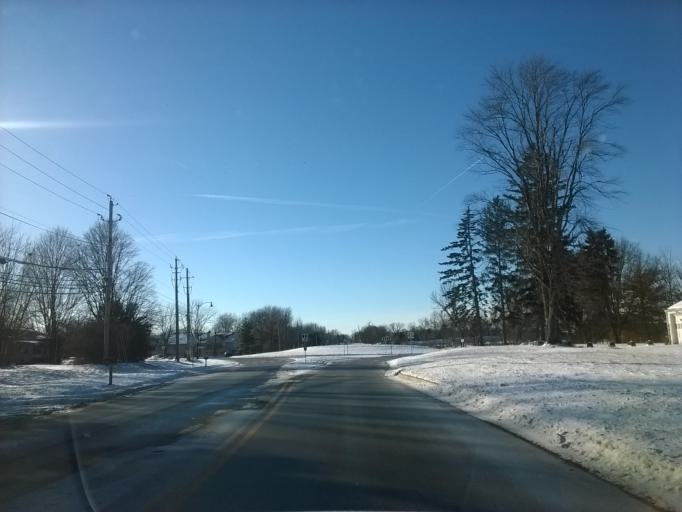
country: US
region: Indiana
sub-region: Marion County
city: Meridian Hills
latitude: 39.9268
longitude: -86.2013
